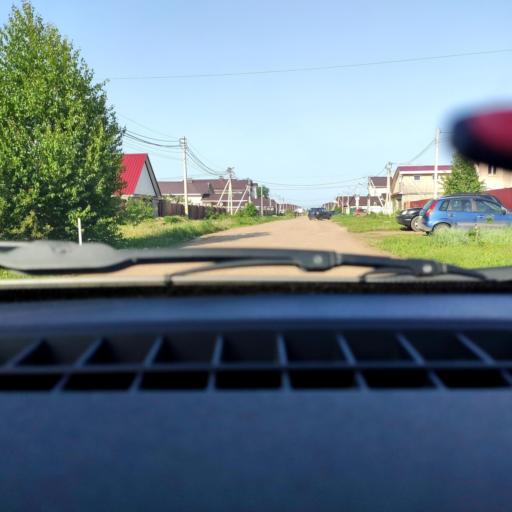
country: RU
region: Bashkortostan
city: Iglino
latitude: 54.8184
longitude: 56.4309
